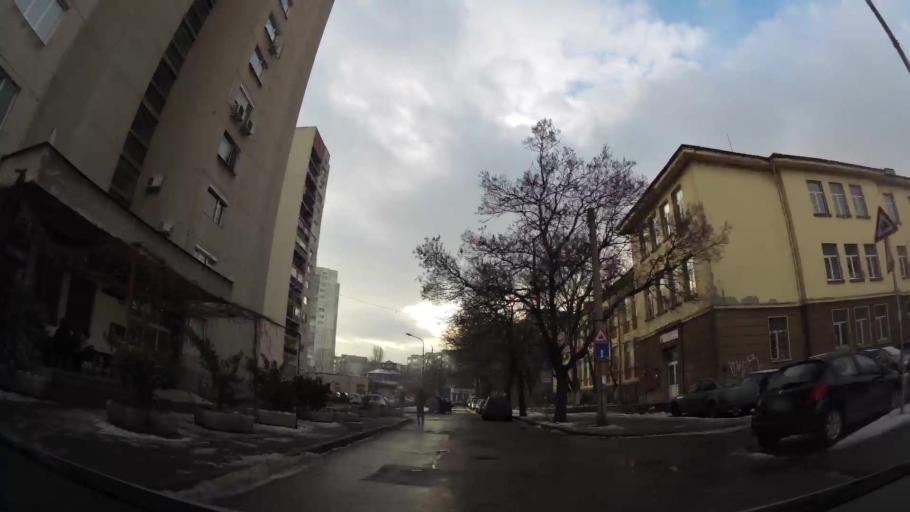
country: BG
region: Sofia-Capital
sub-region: Stolichna Obshtina
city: Sofia
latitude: 42.6967
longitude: 23.2853
